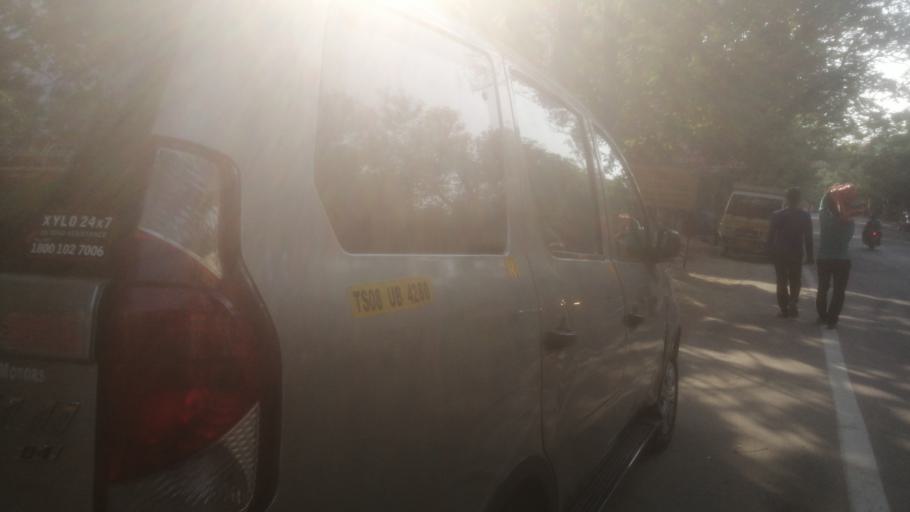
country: IN
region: Telangana
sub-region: Rangareddi
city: Kukatpalli
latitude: 17.5119
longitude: 78.3639
